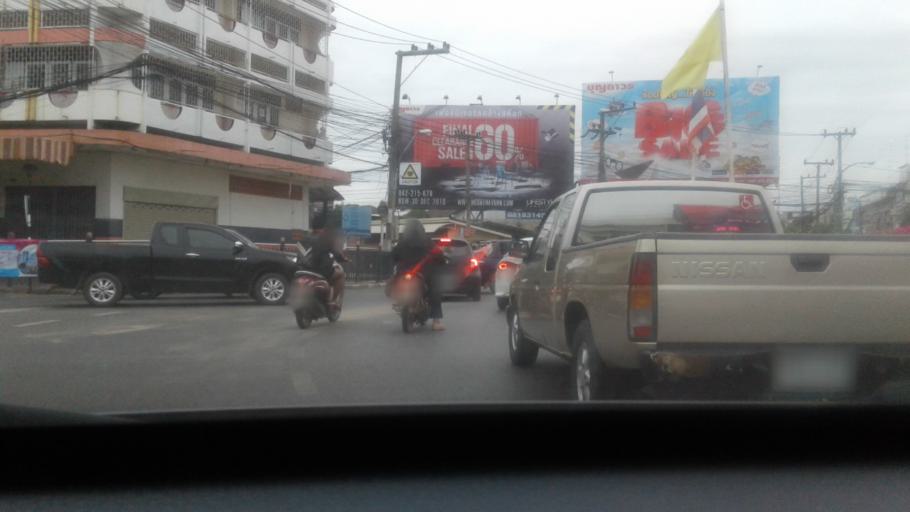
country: TH
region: Changwat Udon Thani
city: Udon Thani
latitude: 17.4009
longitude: 102.7946
